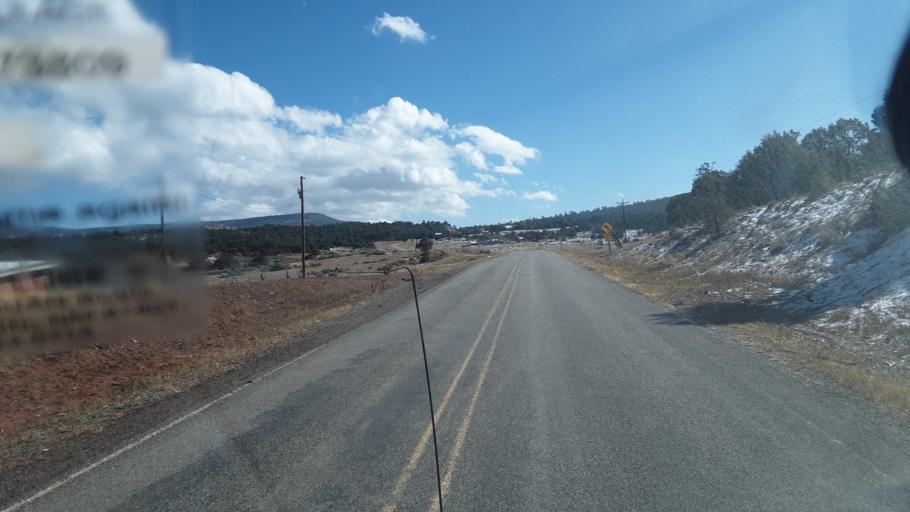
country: US
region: New Mexico
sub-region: Rio Arriba County
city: Santa Teresa
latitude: 36.2339
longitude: -106.8403
